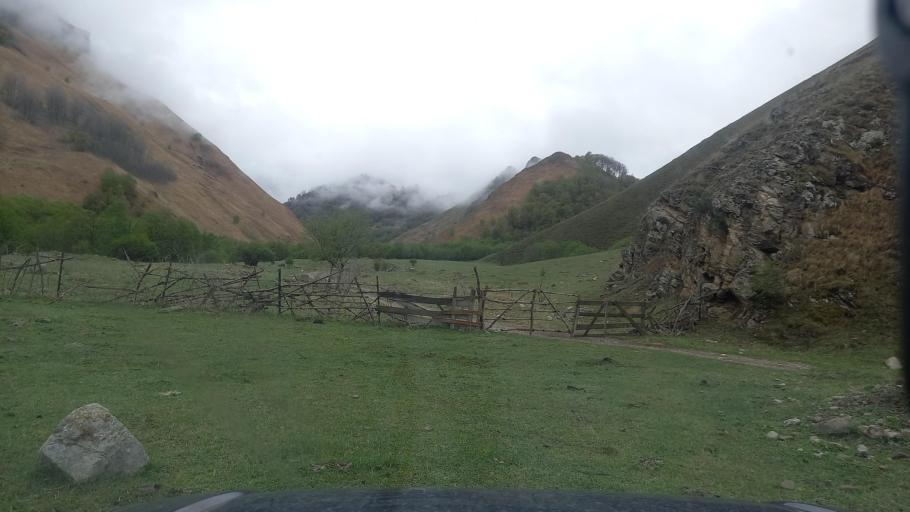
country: RU
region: Kabardino-Balkariya
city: Bylym
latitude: 43.4130
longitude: 43.0399
